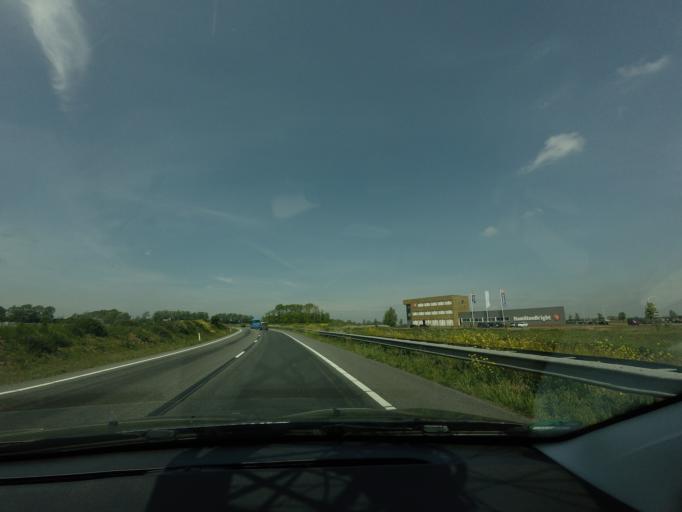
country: NL
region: Friesland
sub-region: Sudwest Fryslan
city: IJlst
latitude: 53.0384
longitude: 5.6184
